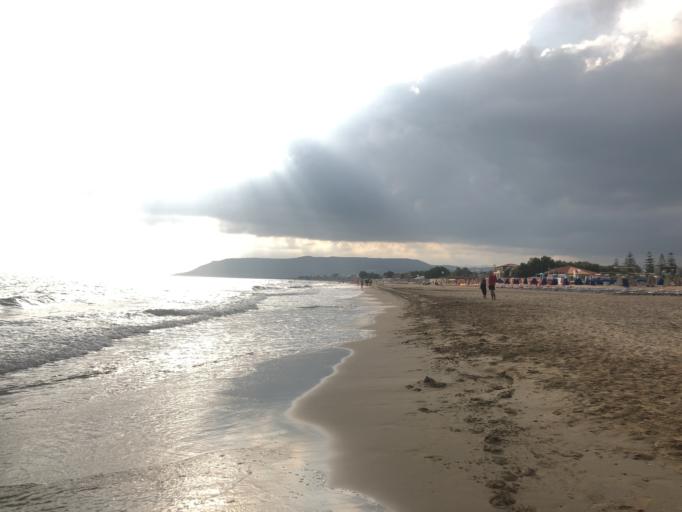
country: GR
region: Crete
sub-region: Nomos Chanias
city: Georgioupolis
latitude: 35.3544
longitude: 24.2930
